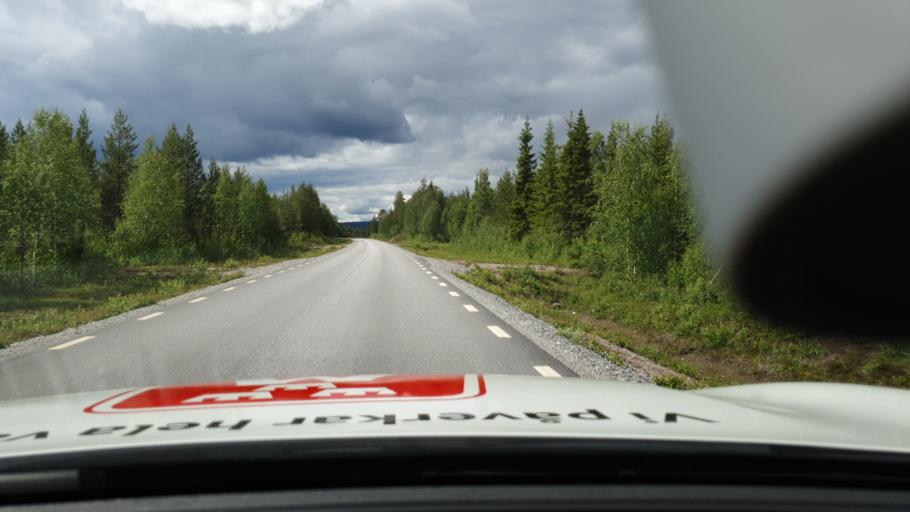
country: SE
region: Norrbotten
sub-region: Jokkmokks Kommun
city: Jokkmokk
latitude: 66.8225
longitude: 19.1816
